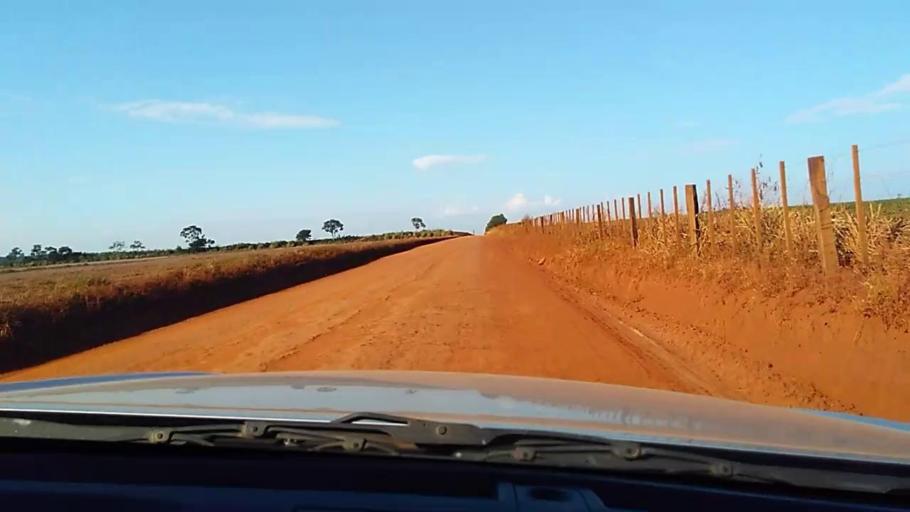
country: PY
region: Alto Parana
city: Naranjal
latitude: -25.7125
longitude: -55.3913
